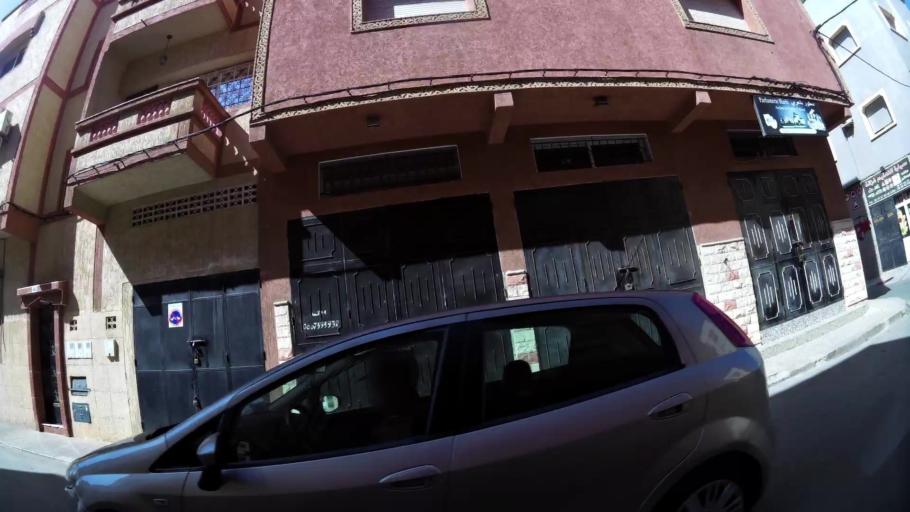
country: MA
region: Rabat-Sale-Zemmour-Zaer
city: Sale
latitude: 34.0671
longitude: -6.7986
